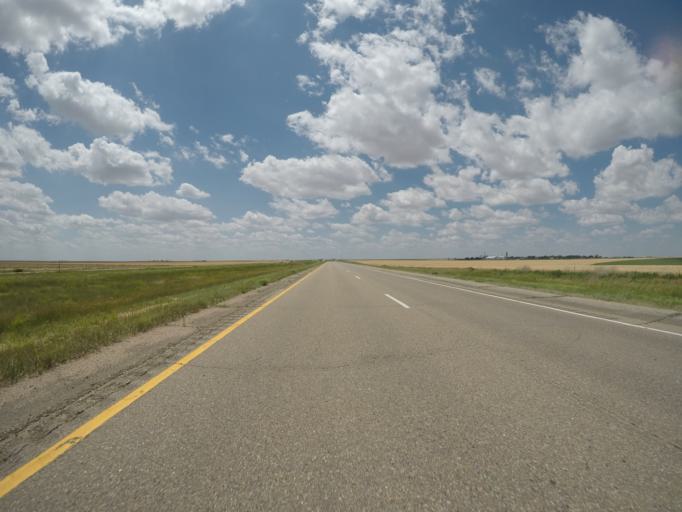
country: US
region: Colorado
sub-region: Kit Carson County
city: Burlington
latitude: 39.2943
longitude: -102.4067
